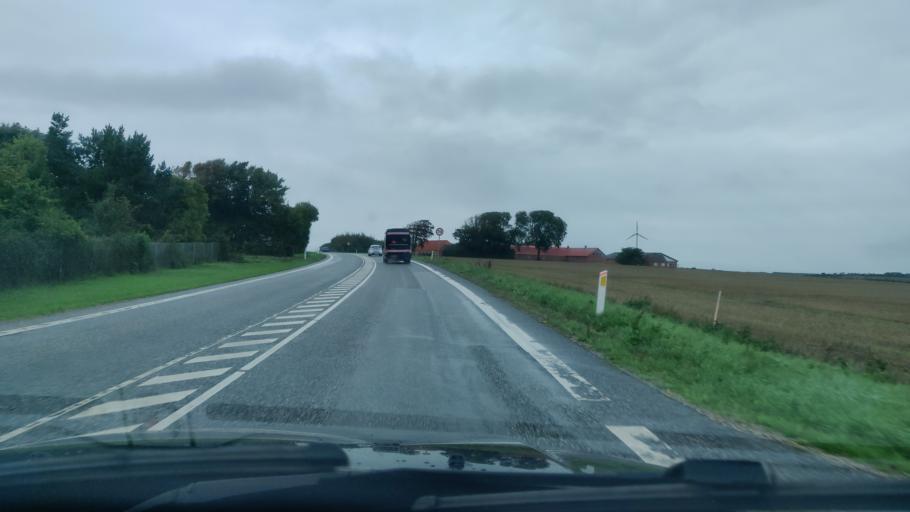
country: DK
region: North Denmark
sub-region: Thisted Kommune
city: Thisted
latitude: 56.9856
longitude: 8.7689
